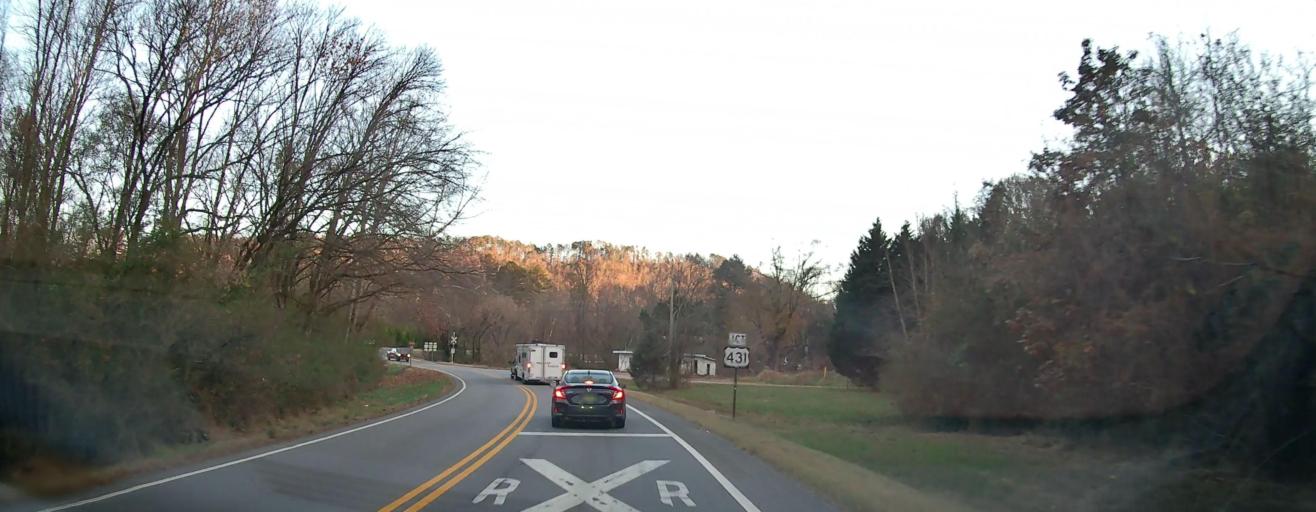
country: US
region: Alabama
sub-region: Etowah County
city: Attalla
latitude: 34.0376
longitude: -86.1130
